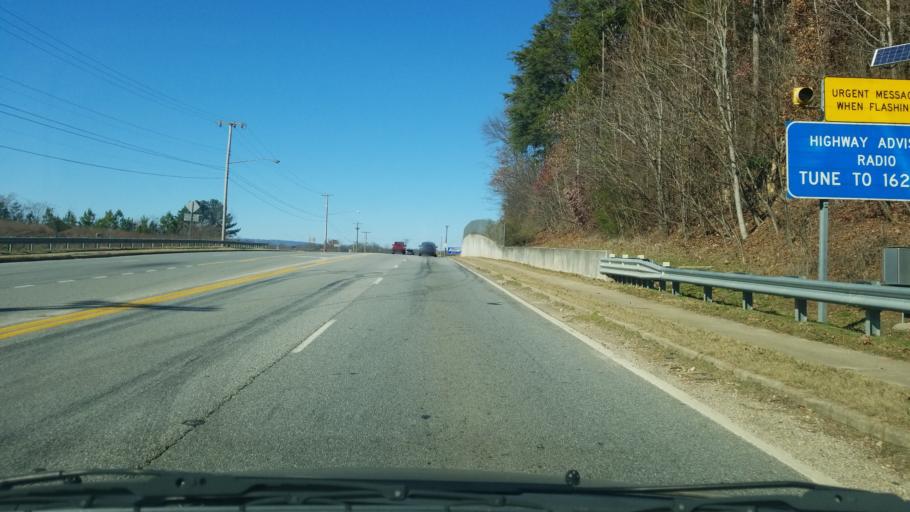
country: US
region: Georgia
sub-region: Catoosa County
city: Indian Springs
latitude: 34.9865
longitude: -85.1885
